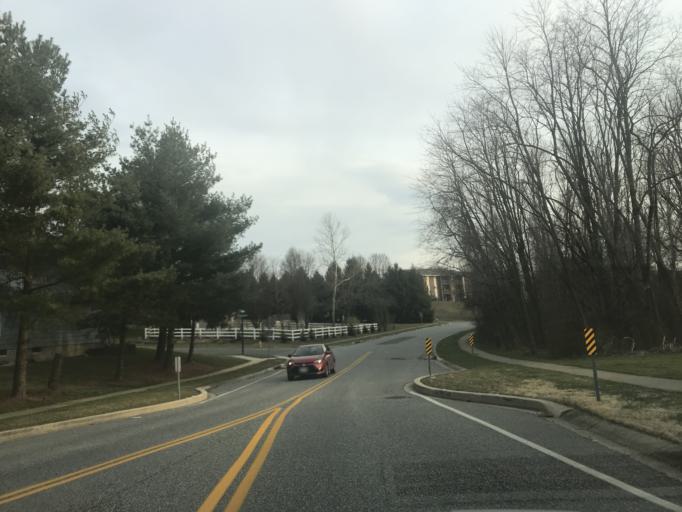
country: US
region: Maryland
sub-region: Harford County
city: South Bel Air
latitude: 39.5431
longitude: -76.3206
